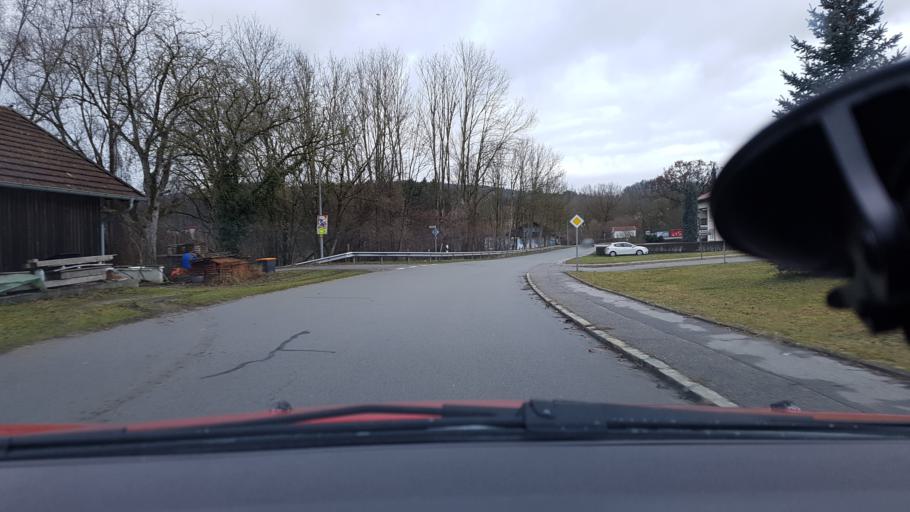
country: DE
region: Bavaria
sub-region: Lower Bavaria
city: Stubenberg
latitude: 48.2864
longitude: 13.0780
